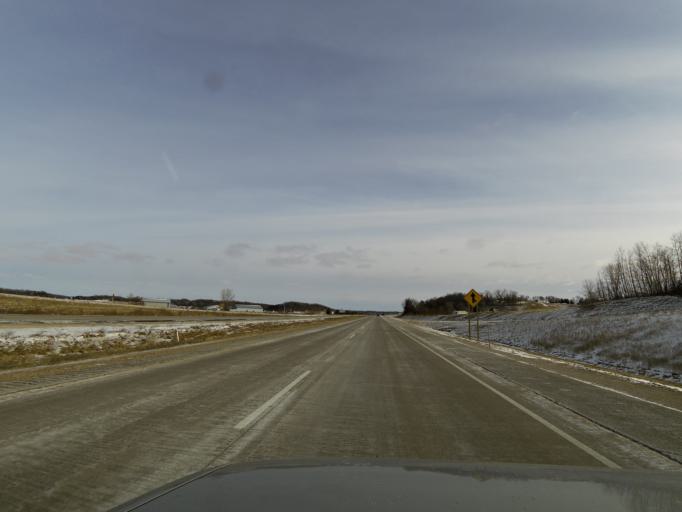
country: US
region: Wisconsin
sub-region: Pierce County
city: River Falls
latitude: 44.8977
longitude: -92.6475
